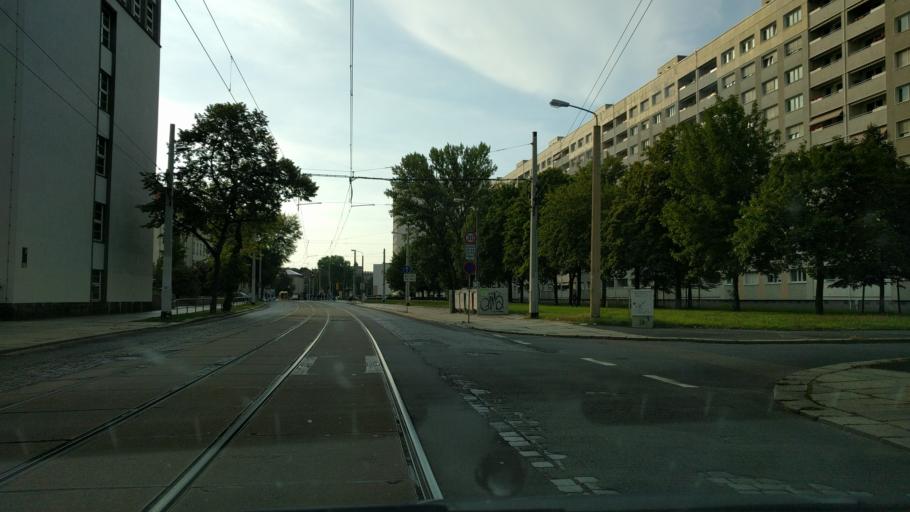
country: DE
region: Saxony
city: Dresden
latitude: 51.0531
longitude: 13.7658
